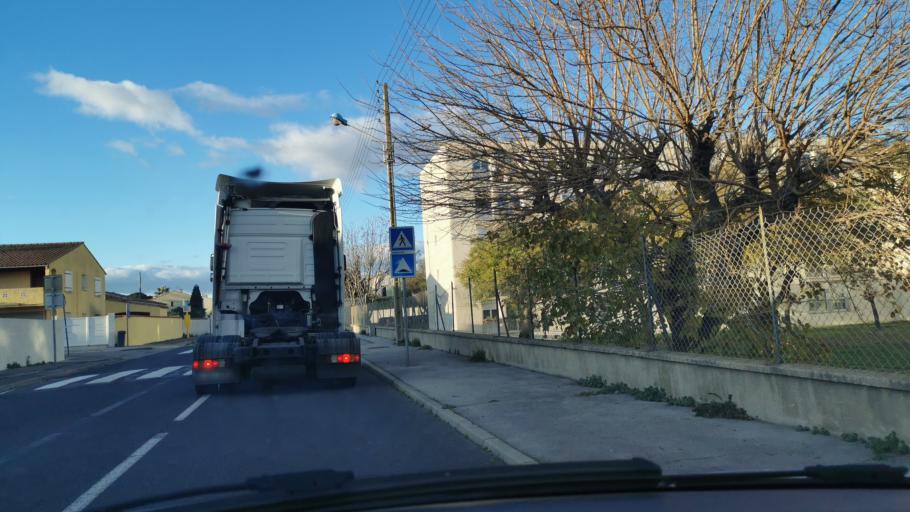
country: FR
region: Languedoc-Roussillon
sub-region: Departement de l'Herault
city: Frontignan
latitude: 43.4295
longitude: 3.7256
